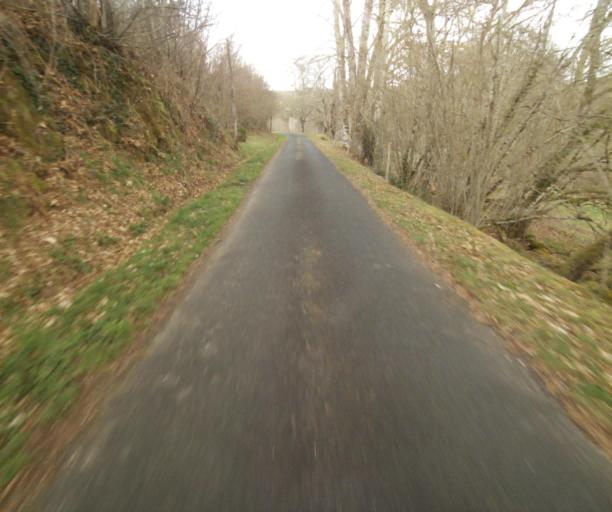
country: FR
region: Limousin
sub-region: Departement de la Correze
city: Egletons
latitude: 45.2653
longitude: 1.9944
